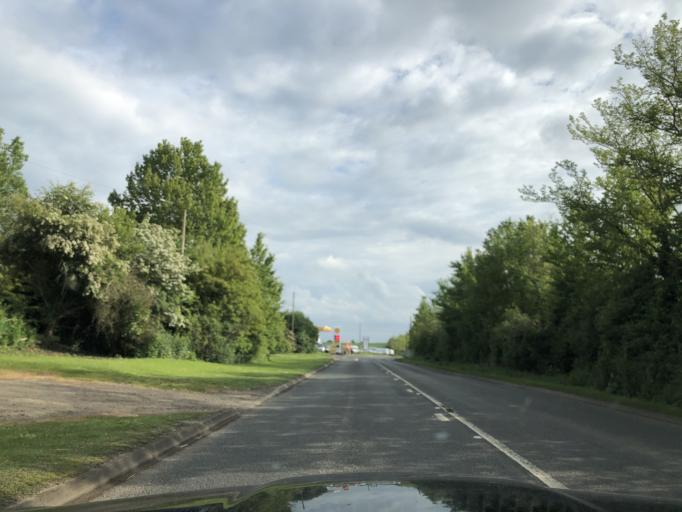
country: GB
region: England
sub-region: Warwickshire
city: Shipston on Stour
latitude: 52.0511
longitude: -1.6649
